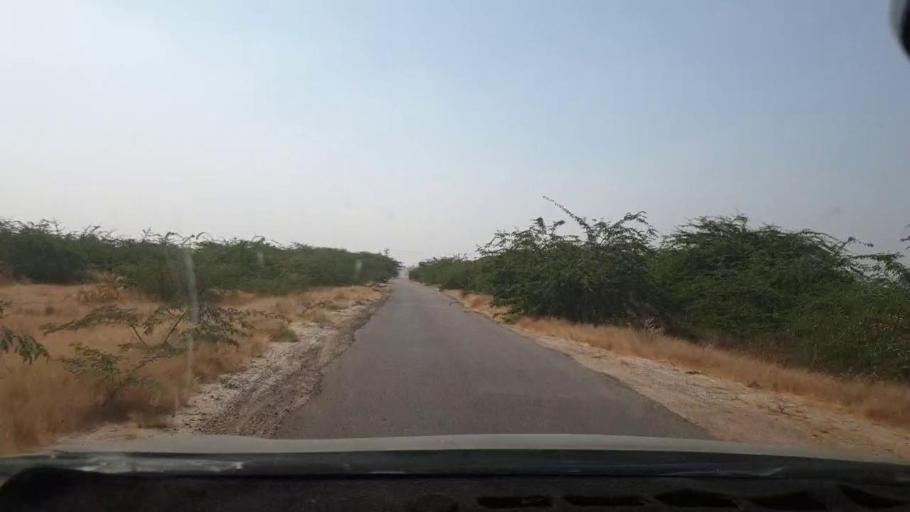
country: PK
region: Sindh
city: Malir Cantonment
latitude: 25.0987
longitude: 67.1910
